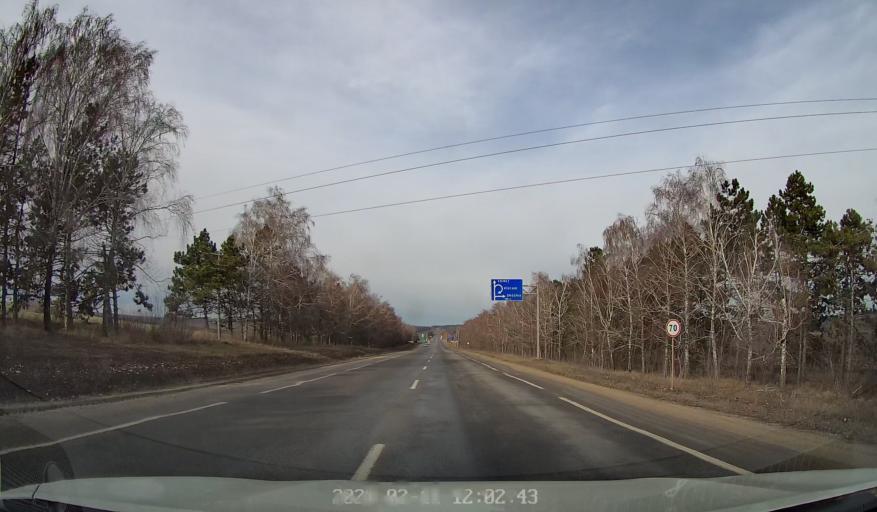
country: MD
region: Riscani
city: Riscani
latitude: 47.9529
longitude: 27.6187
